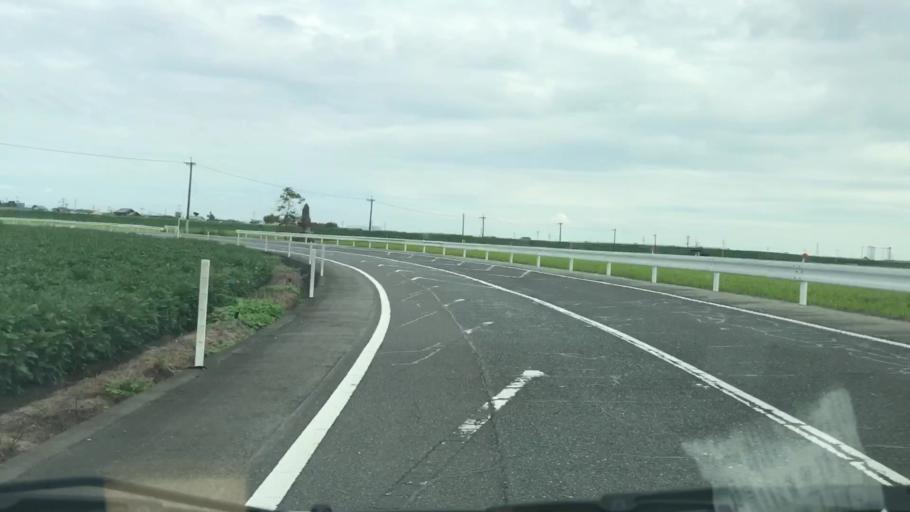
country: JP
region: Saga Prefecture
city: Saga-shi
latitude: 33.2890
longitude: 130.2405
